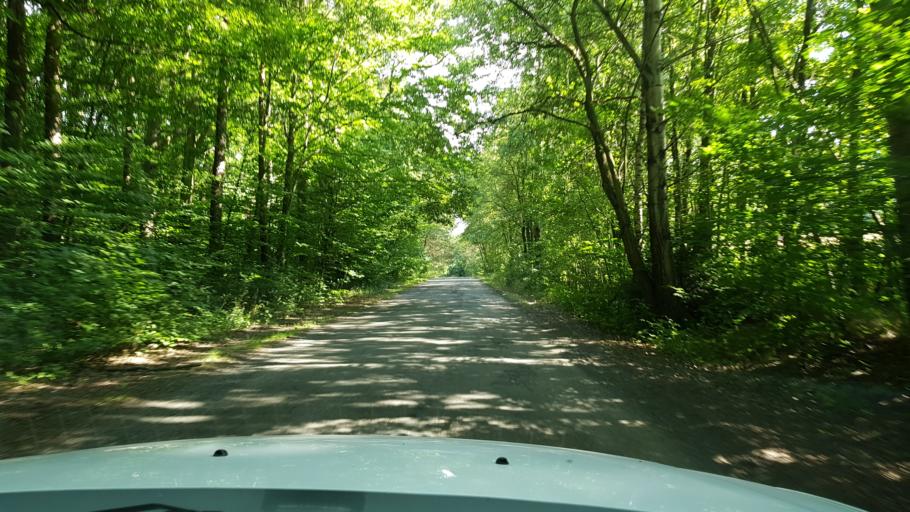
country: PL
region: West Pomeranian Voivodeship
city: Trzcinsko Zdroj
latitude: 52.9433
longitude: 14.5513
